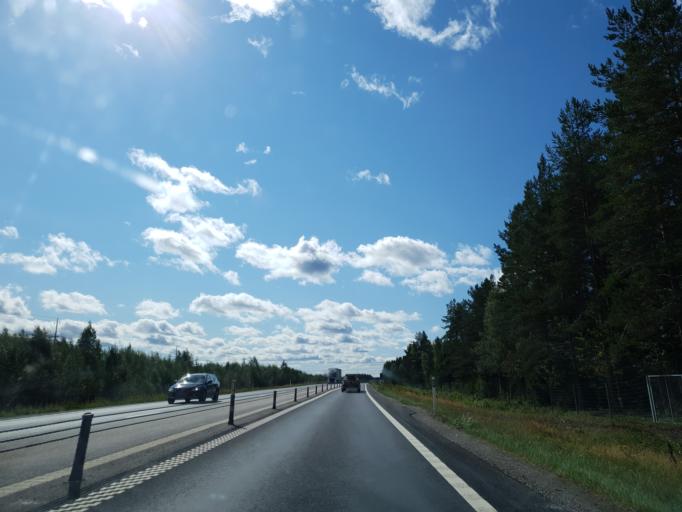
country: SE
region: Vaesterbotten
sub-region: Nordmalings Kommun
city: Nordmaling
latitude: 63.5616
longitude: 19.4278
